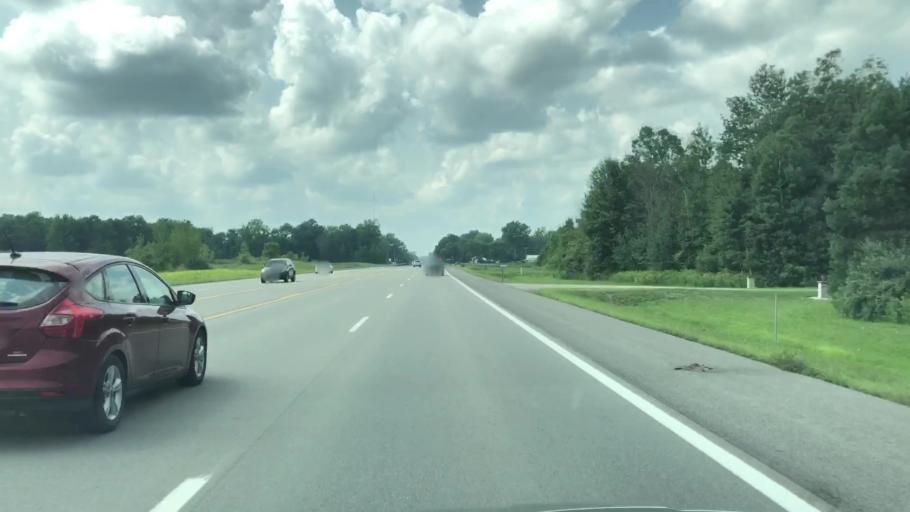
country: US
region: Michigan
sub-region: Midland County
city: Coleman
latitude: 43.6116
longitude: -84.5207
